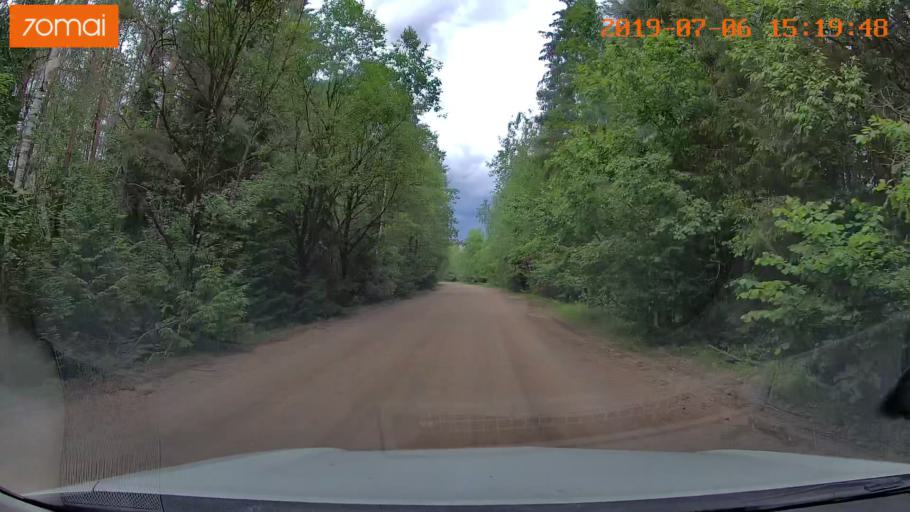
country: BY
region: Minsk
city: Valozhyn
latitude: 54.0010
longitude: 26.6437
